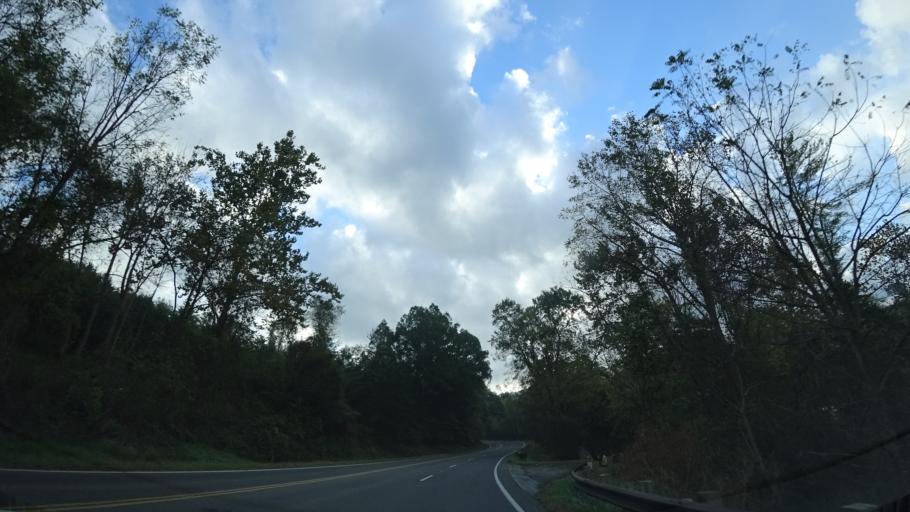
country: US
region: Virginia
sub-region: Page County
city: Luray
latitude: 38.6592
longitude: -78.3669
